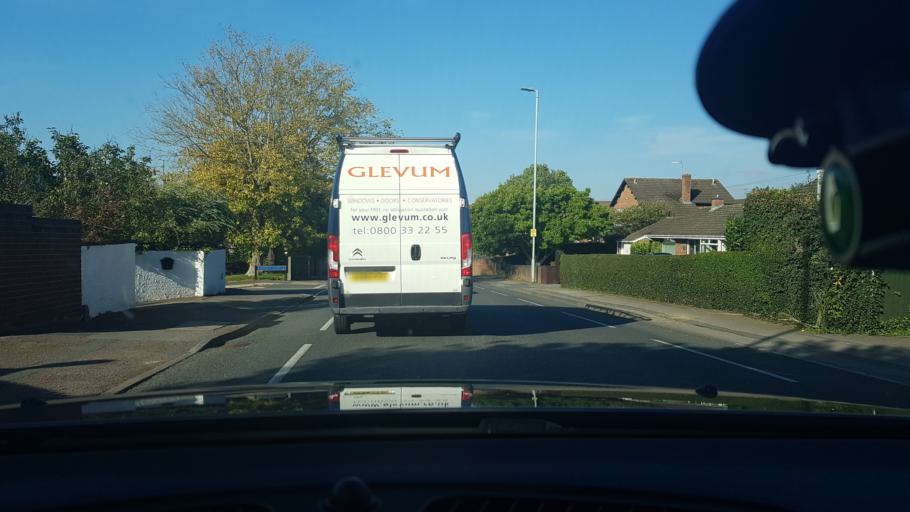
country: GB
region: England
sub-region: Gloucestershire
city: Gloucester
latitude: 51.8376
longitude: -2.2428
